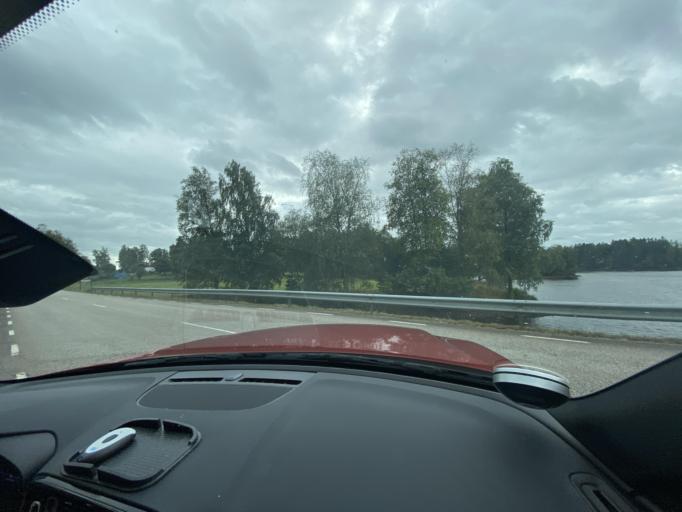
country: SE
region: Kronoberg
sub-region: Markaryds Kommun
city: Markaryd
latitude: 56.4892
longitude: 13.5279
